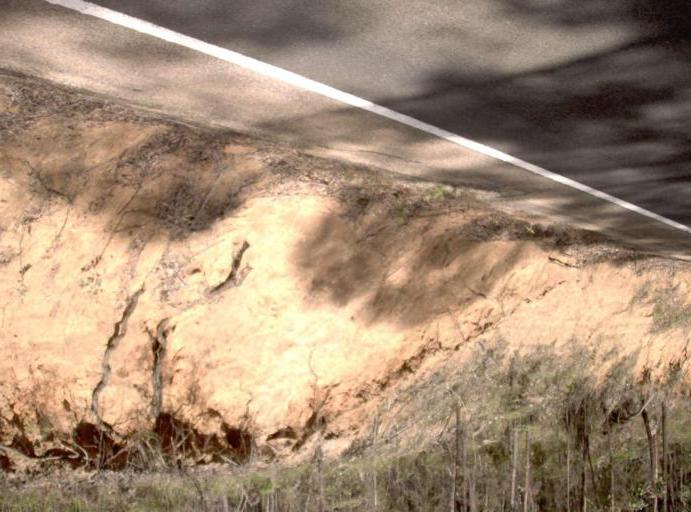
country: AU
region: New South Wales
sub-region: Bombala
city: Bombala
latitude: -37.5487
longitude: 149.3629
